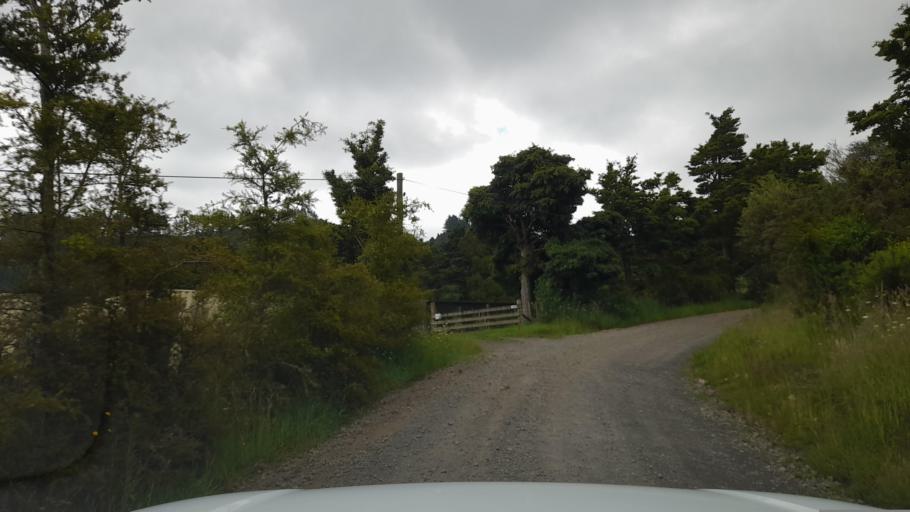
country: NZ
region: Northland
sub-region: Far North District
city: Waimate North
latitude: -35.3972
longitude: 173.7848
